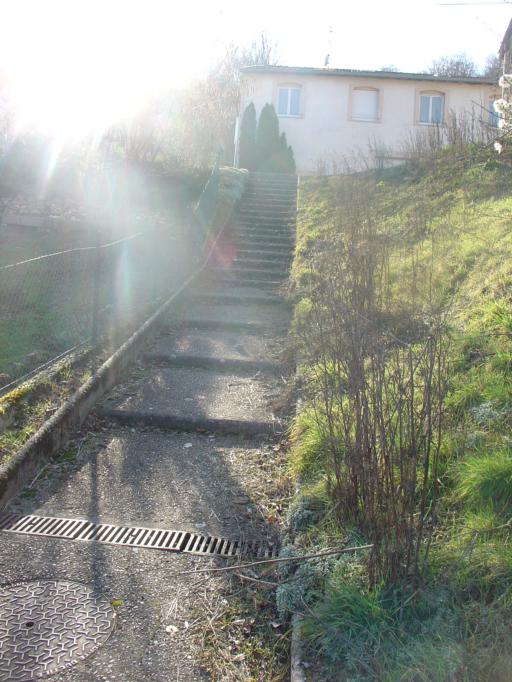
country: FR
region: Lorraine
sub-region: Departement de Meurthe-et-Moselle
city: Foug
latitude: 48.7488
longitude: 5.7592
